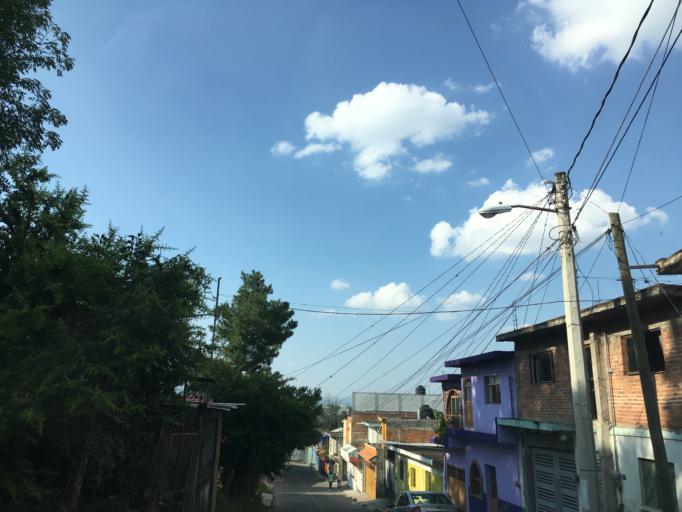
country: MX
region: Michoacan
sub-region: Morelia
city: Morelos
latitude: 19.6489
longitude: -101.2366
